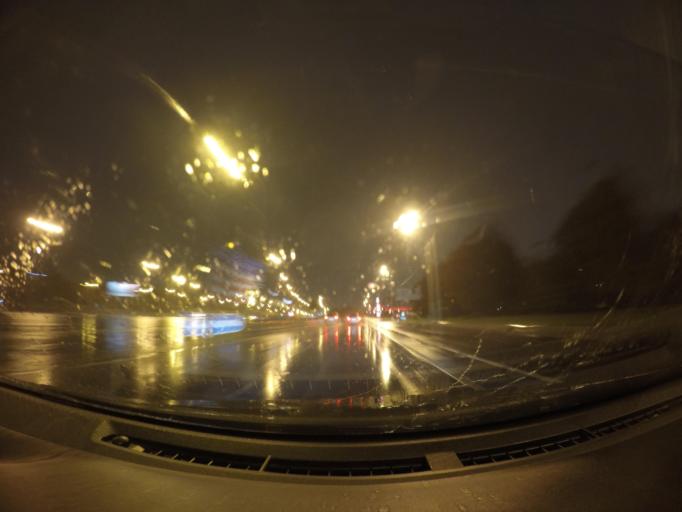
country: RU
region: Moscow
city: Tsaritsyno
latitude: 55.6511
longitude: 37.6586
